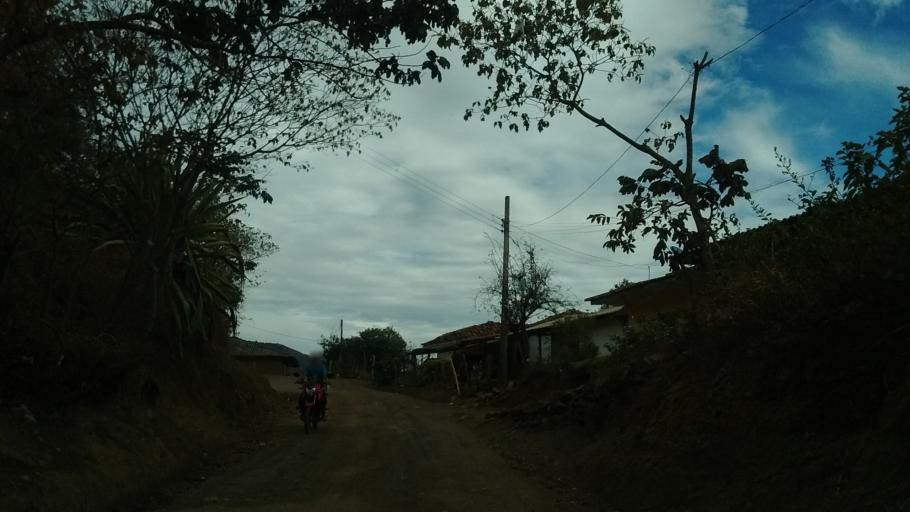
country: CO
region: Cauca
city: Almaguer
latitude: 1.8482
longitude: -76.9023
